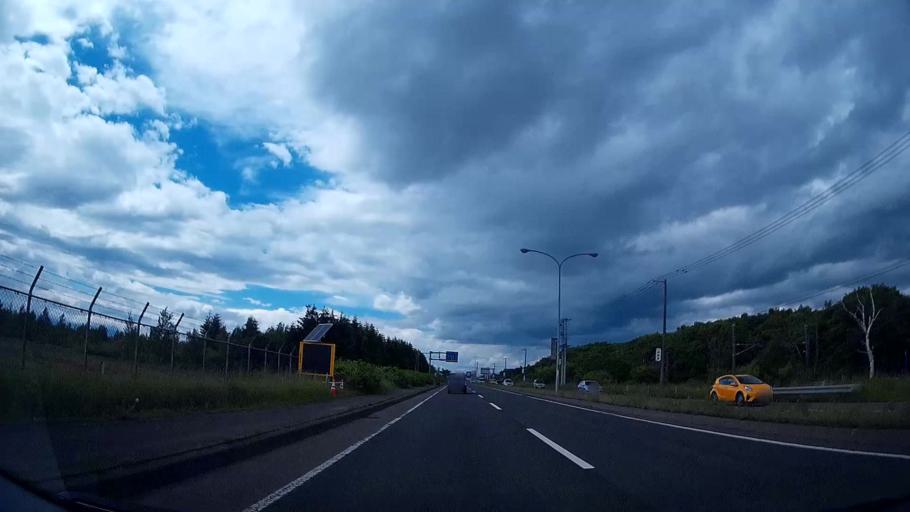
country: JP
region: Hokkaido
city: Chitose
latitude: 42.8156
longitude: 141.6659
